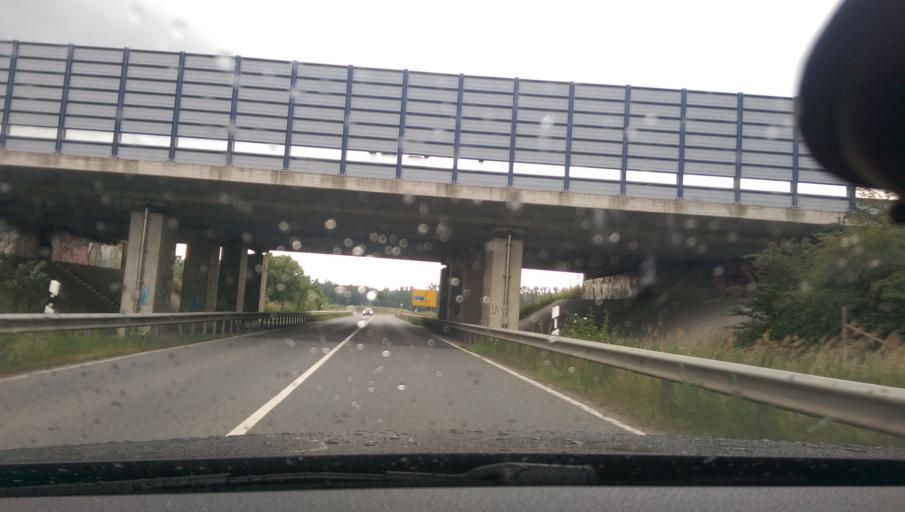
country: DE
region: Lower Saxony
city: Cremlingen
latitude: 52.2551
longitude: 10.6576
